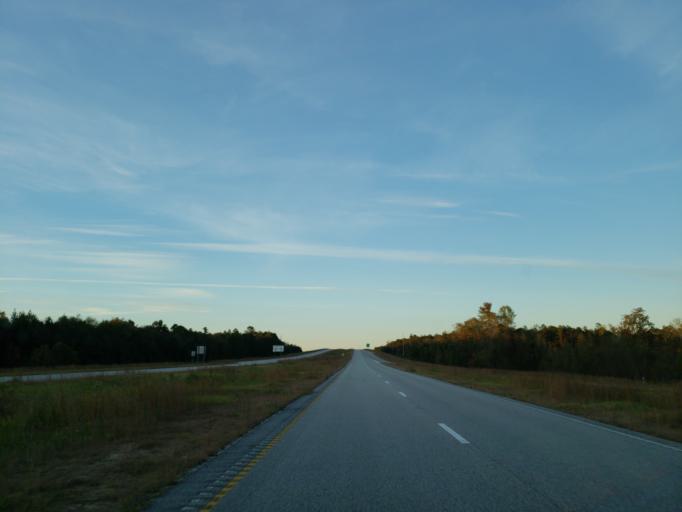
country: US
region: Mississippi
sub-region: Wayne County
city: Belmont
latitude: 31.4387
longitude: -88.4654
